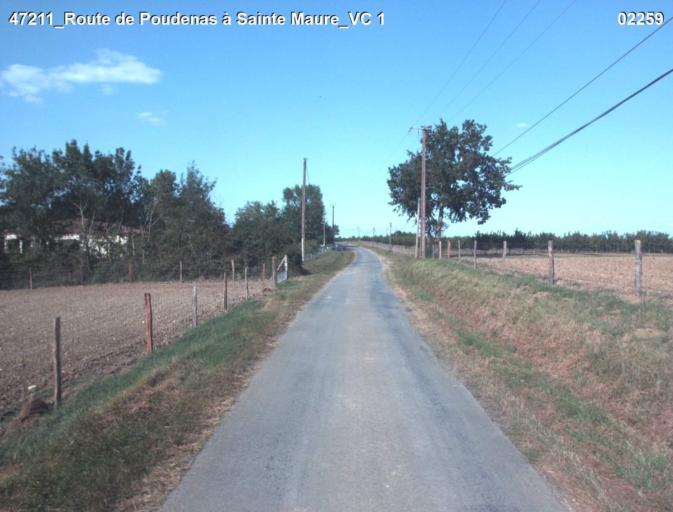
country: FR
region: Aquitaine
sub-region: Departement du Lot-et-Garonne
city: Mezin
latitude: 44.0303
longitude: 0.2037
